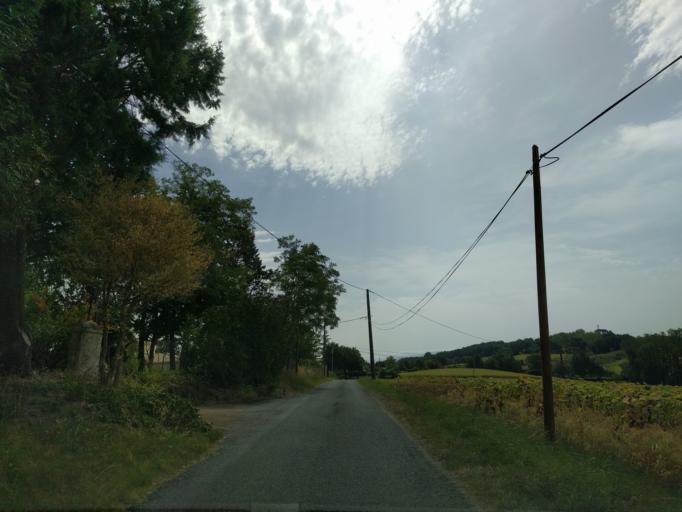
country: FR
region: Midi-Pyrenees
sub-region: Departement du Tarn
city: Castres
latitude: 43.6386
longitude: 2.2075
